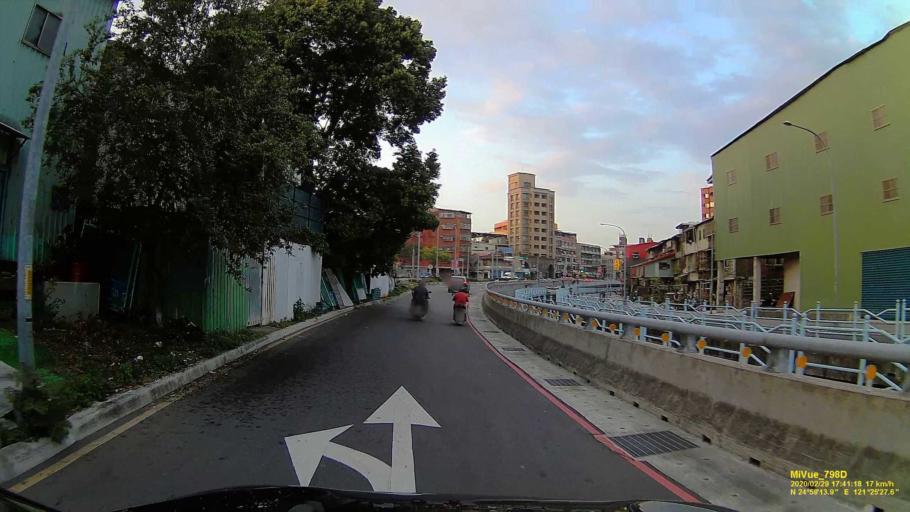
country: TW
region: Taipei
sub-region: Taipei
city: Banqiao
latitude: 24.9874
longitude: 121.4243
